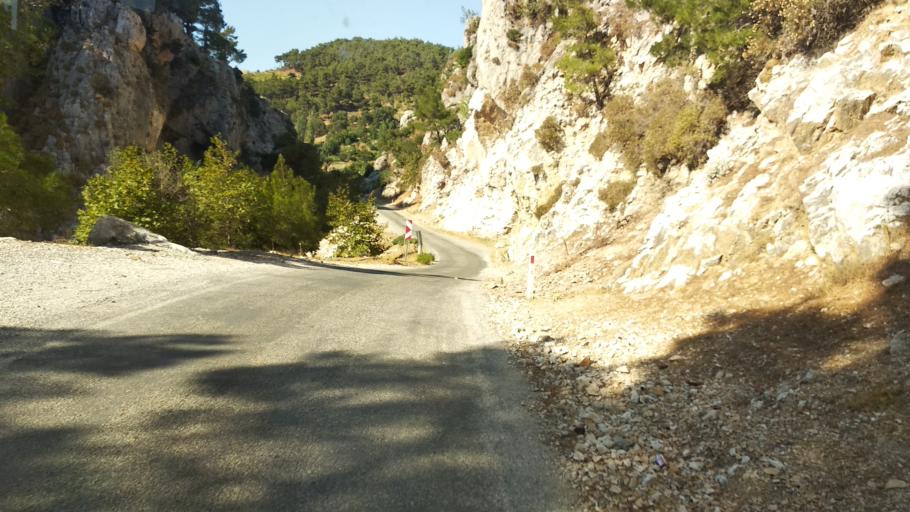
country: TR
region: Izmir
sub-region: Seferihisar
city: Seferhisar
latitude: 38.3211
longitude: 26.9571
